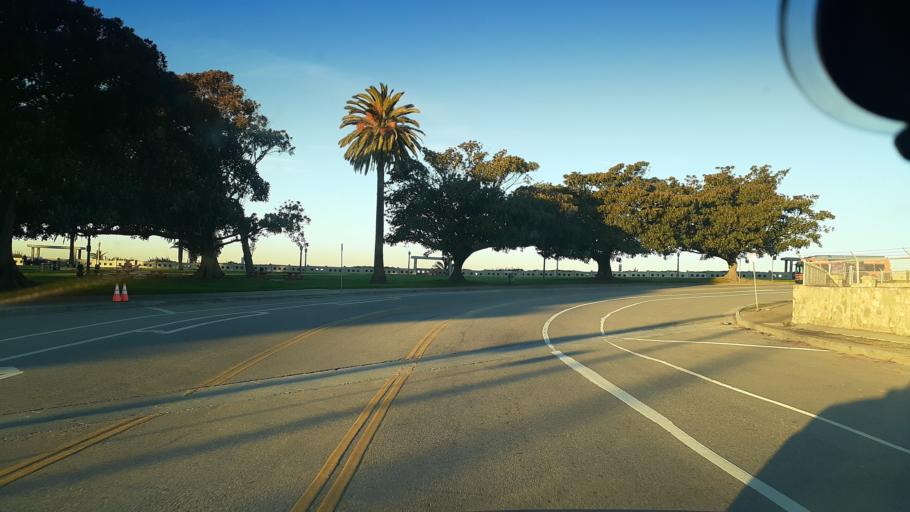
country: US
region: California
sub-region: Los Angeles County
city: San Pedro
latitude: 33.7070
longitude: -118.2936
